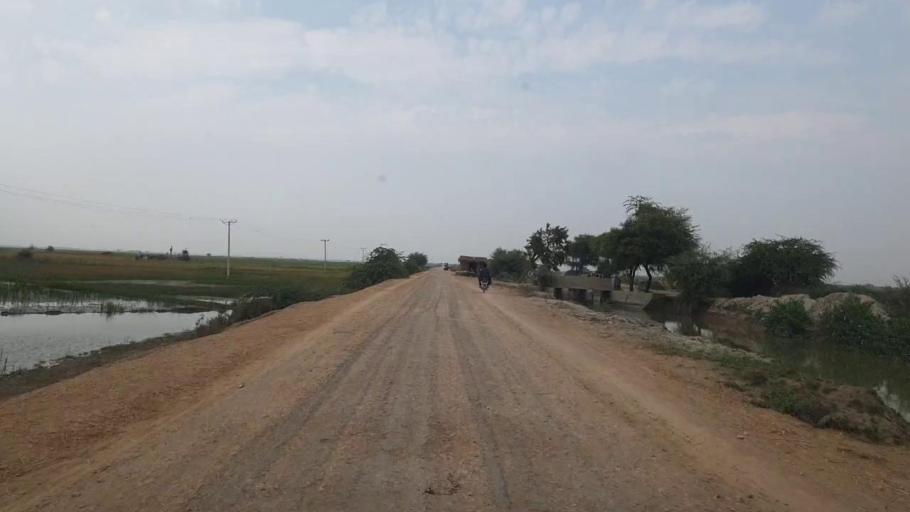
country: PK
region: Sindh
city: Kario
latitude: 24.6098
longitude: 68.5933
